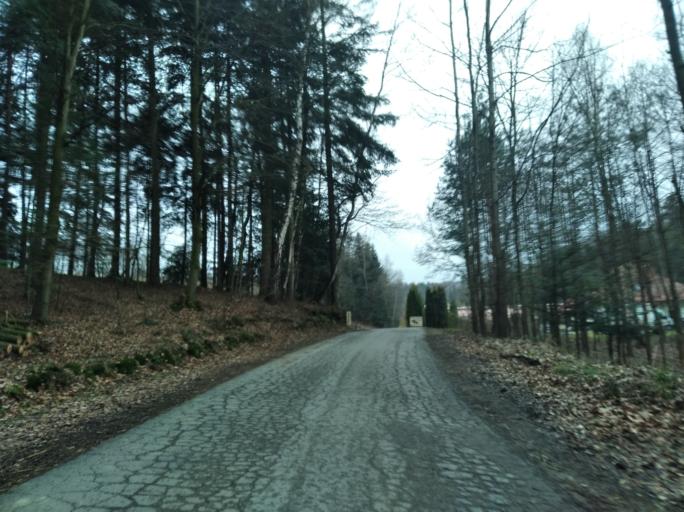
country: PL
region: Subcarpathian Voivodeship
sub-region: Powiat strzyzowski
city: Strzyzow
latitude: 49.8937
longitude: 21.8121
